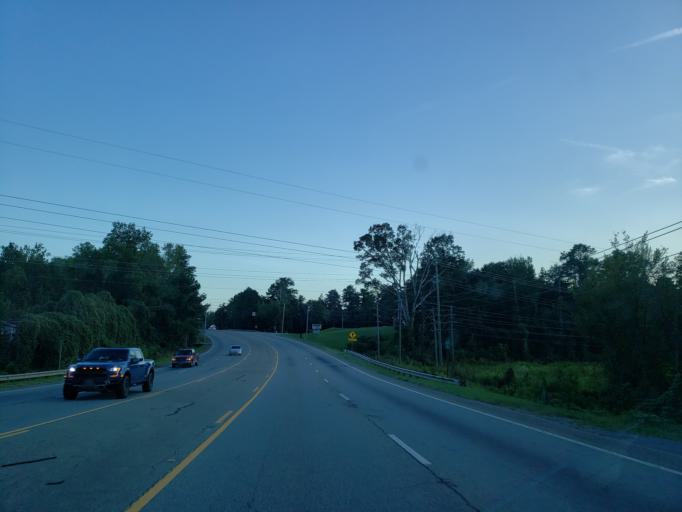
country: US
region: Georgia
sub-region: Floyd County
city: Lindale
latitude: 34.1813
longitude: -85.2057
